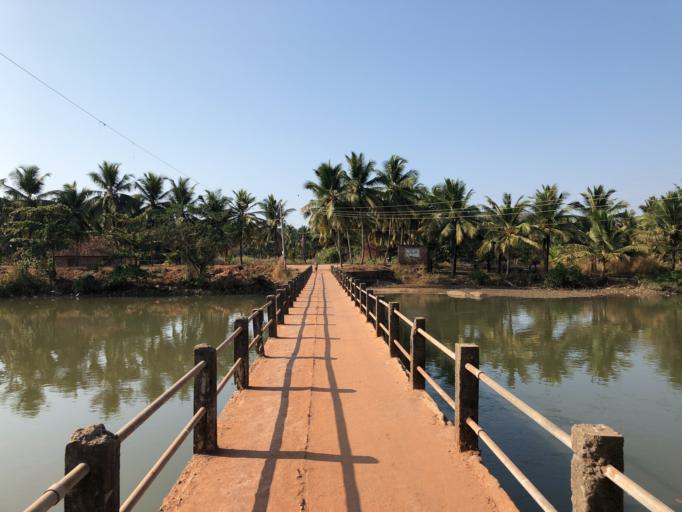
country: IN
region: Karnataka
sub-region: Dakshina Kannada
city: Mangalore
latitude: 12.9049
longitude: 74.8218
